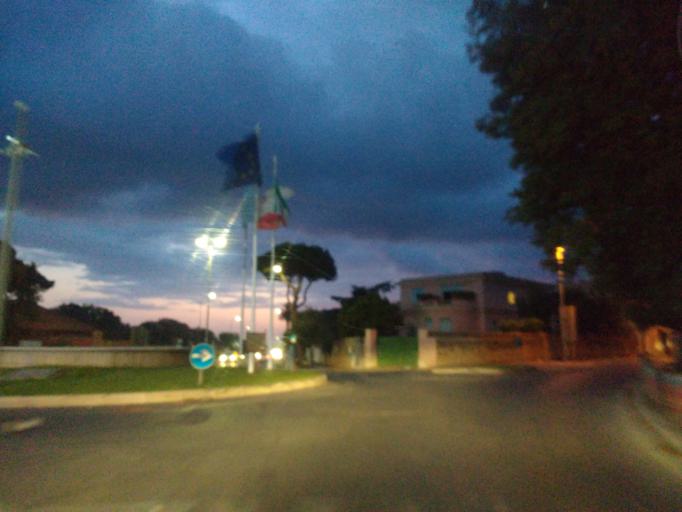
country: IT
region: Latium
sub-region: Citta metropolitana di Roma Capitale
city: Anzio
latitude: 41.4510
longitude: 12.6258
